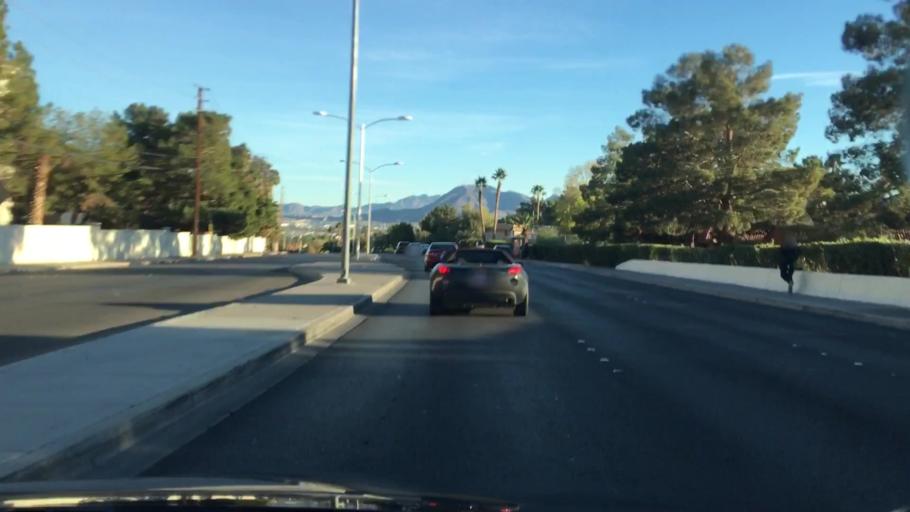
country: US
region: Nevada
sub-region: Clark County
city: Whitney
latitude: 36.0666
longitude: -115.0668
